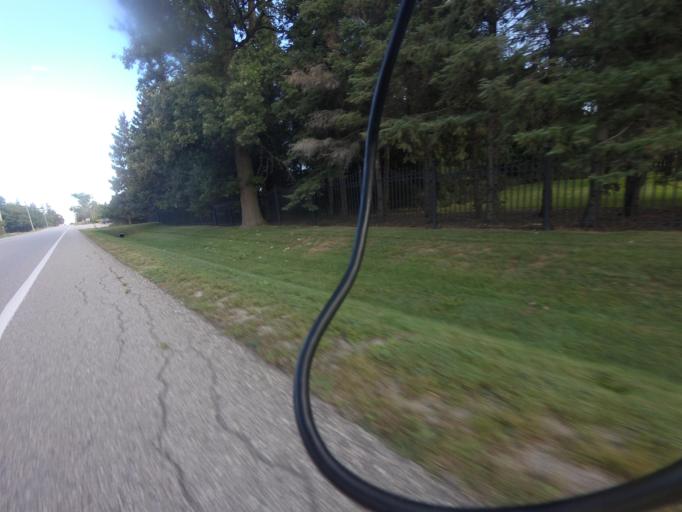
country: CA
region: Ontario
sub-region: Wellington County
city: Guelph
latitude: 43.5783
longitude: -80.3333
